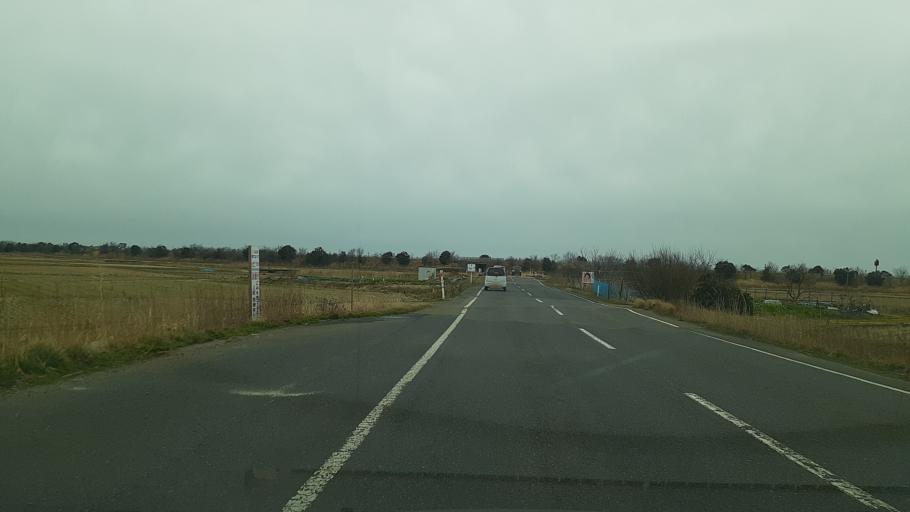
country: JP
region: Niigata
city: Niitsu-honcho
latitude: 37.8192
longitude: 139.0844
